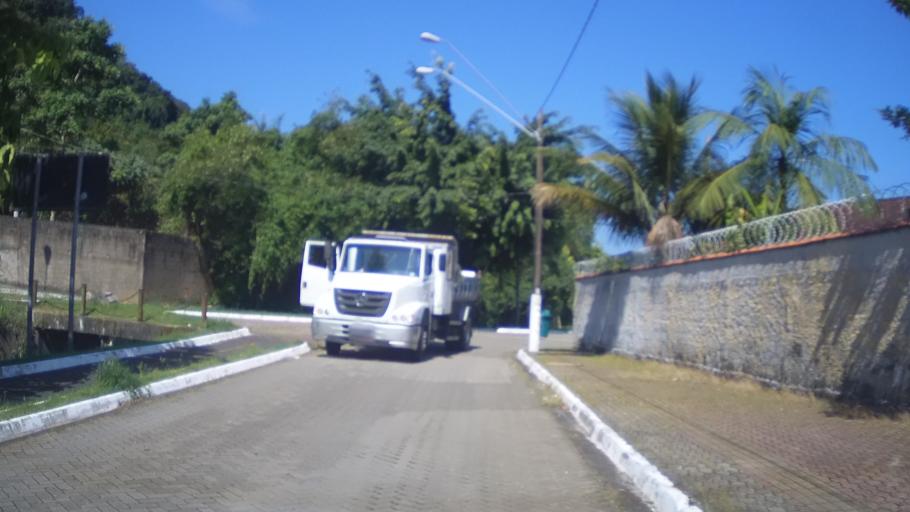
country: BR
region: Sao Paulo
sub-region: Praia Grande
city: Praia Grande
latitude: -24.0037
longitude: -46.4012
